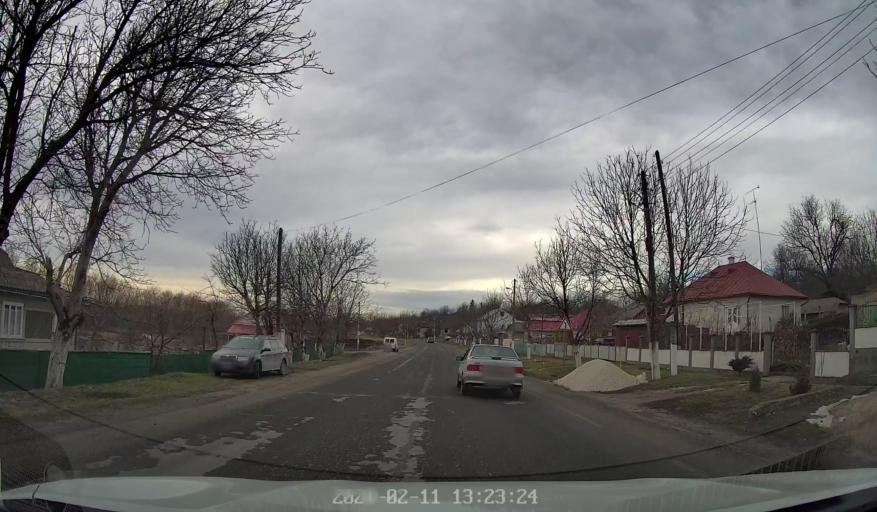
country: RO
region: Botosani
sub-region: Comuna Paltinis
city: Paltinis
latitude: 48.2706
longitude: 26.6810
